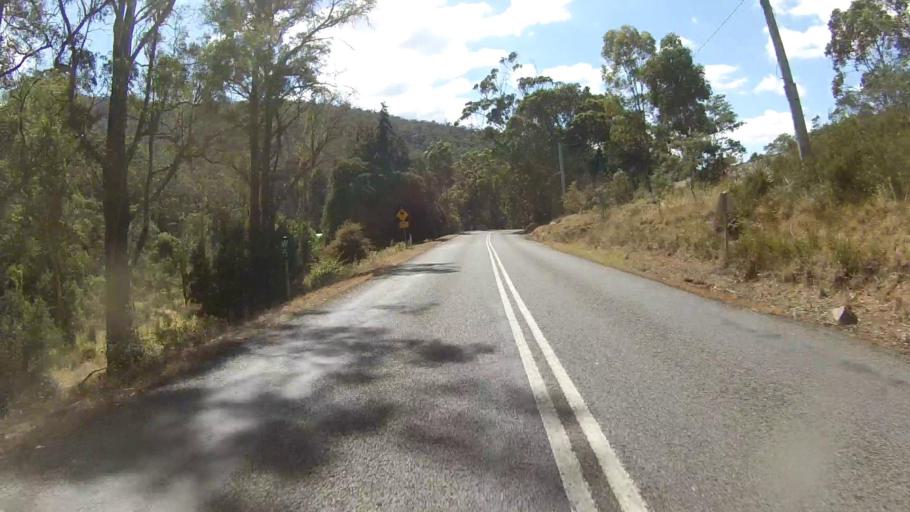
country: AU
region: Tasmania
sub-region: Derwent Valley
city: New Norfolk
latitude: -42.6814
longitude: 146.7456
